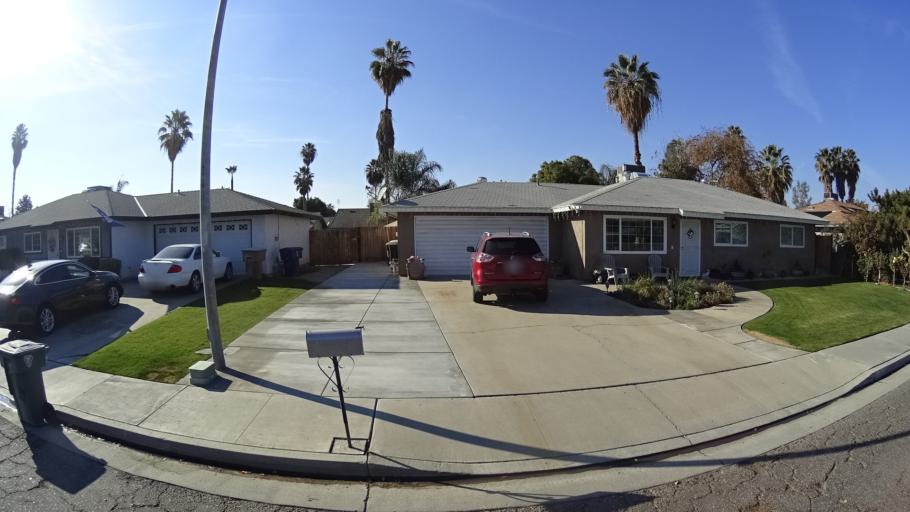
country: US
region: California
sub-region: Kern County
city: Greenfield
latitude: 35.3013
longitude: -119.0509
